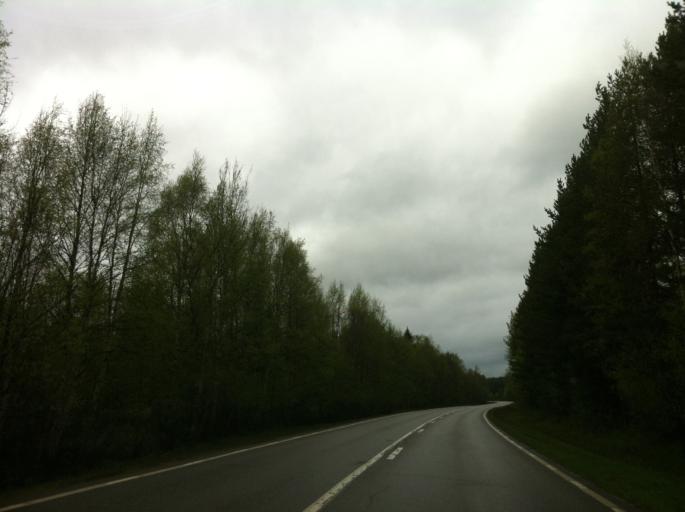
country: SE
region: Jaemtland
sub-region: Harjedalens Kommun
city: Sveg
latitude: 62.1302
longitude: 14.0590
